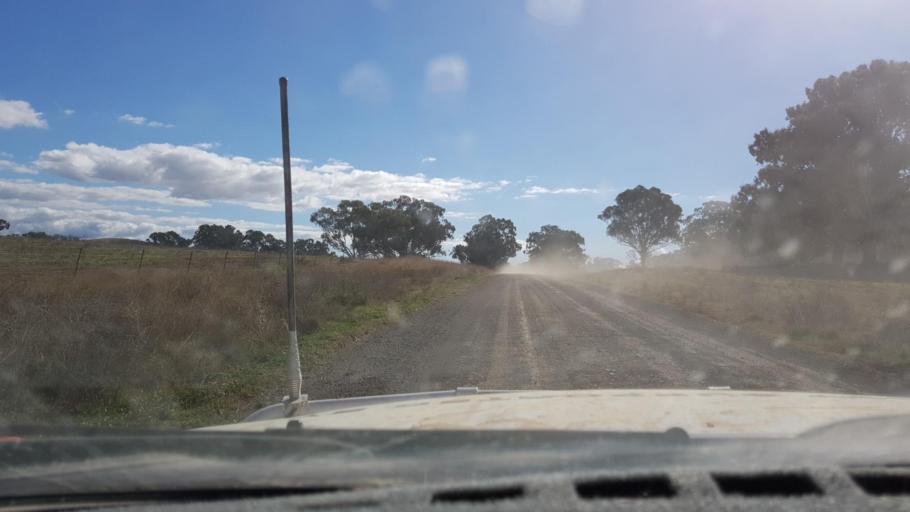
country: AU
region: New South Wales
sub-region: Narrabri
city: Blair Athol
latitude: -30.4362
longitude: 150.4570
